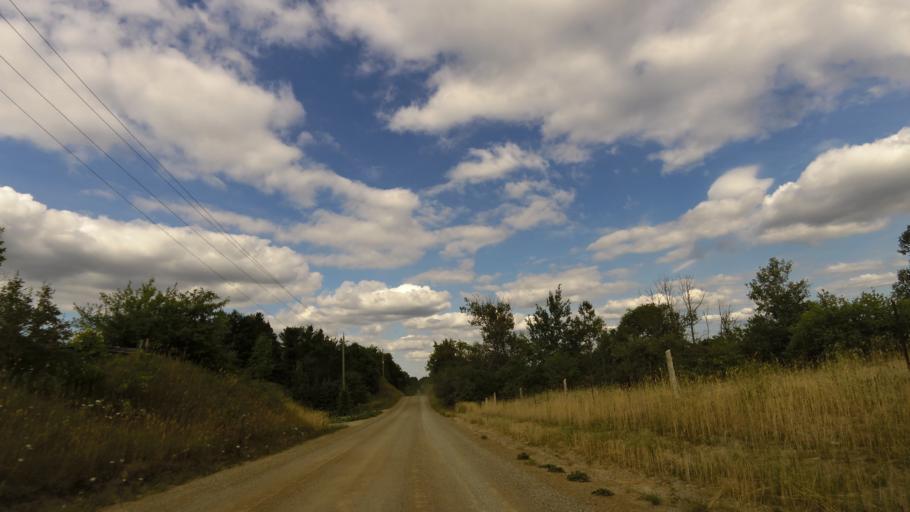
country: CA
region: Ontario
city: Orangeville
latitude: 43.9806
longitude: -79.9479
